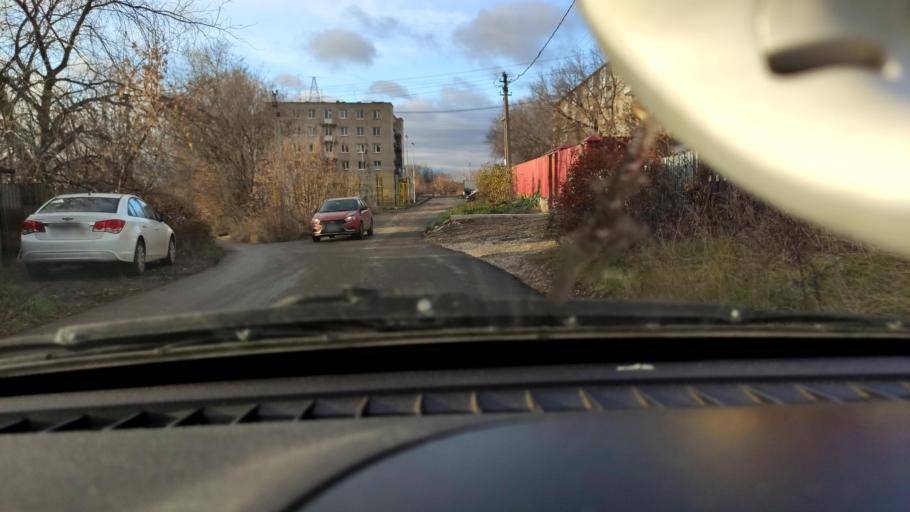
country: RU
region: Perm
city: Kondratovo
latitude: 57.9586
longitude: 56.1500
